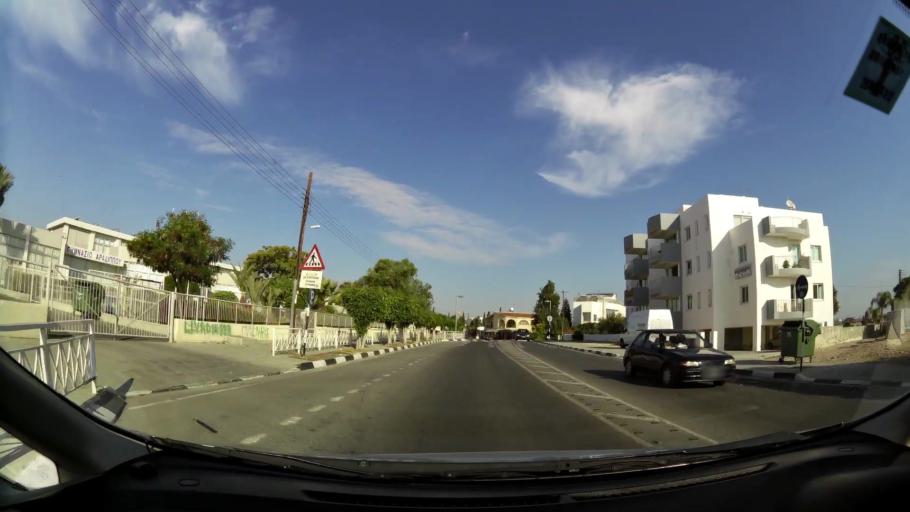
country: CY
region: Larnaka
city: Aradippou
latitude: 34.9437
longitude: 33.5972
